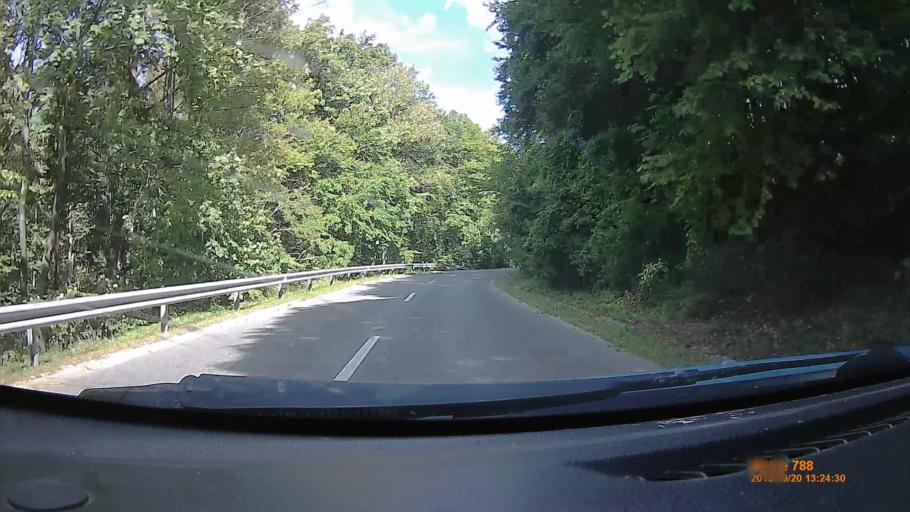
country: HU
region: Heves
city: Felsotarkany
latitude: 48.0387
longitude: 20.4826
